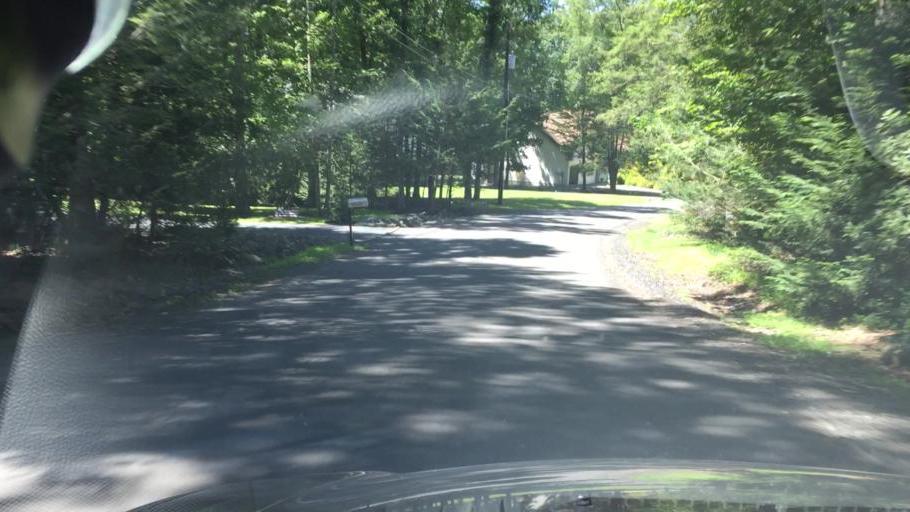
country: US
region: Pennsylvania
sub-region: Luzerne County
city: Freeland
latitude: 41.0374
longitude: -75.9370
